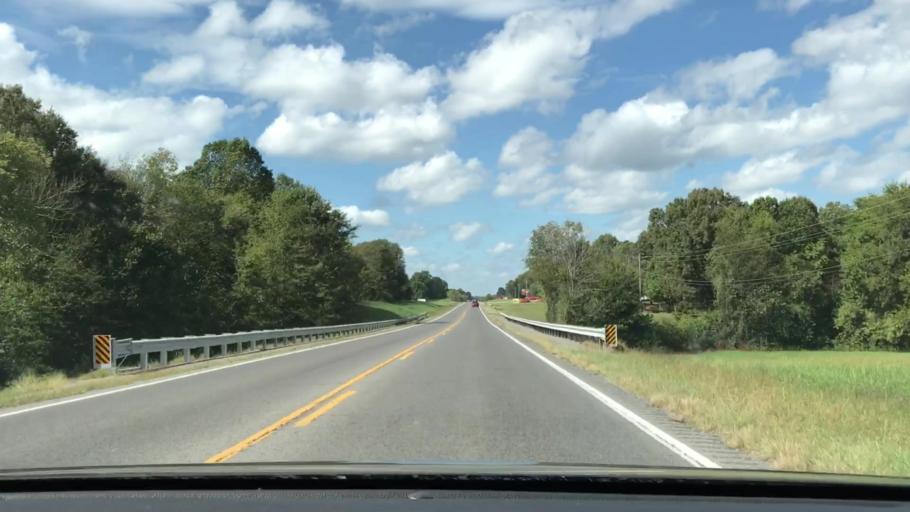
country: US
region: Kentucky
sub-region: Livingston County
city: Ledbetter
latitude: 37.0068
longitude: -88.4582
